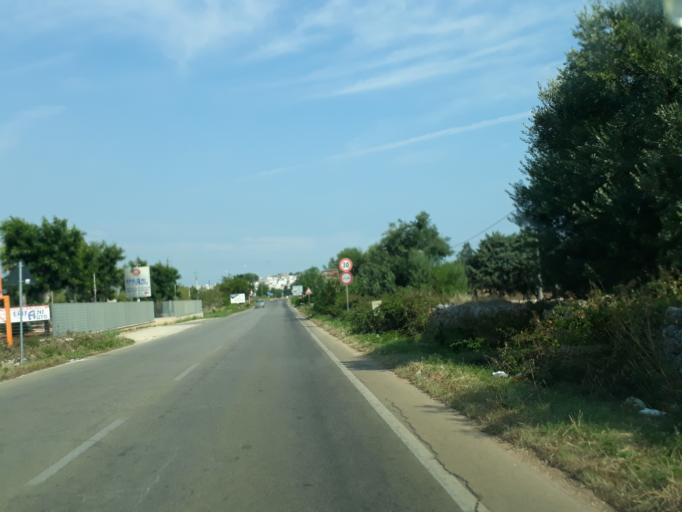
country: IT
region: Apulia
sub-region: Provincia di Brindisi
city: Carovigno
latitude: 40.6936
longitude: 17.6708
